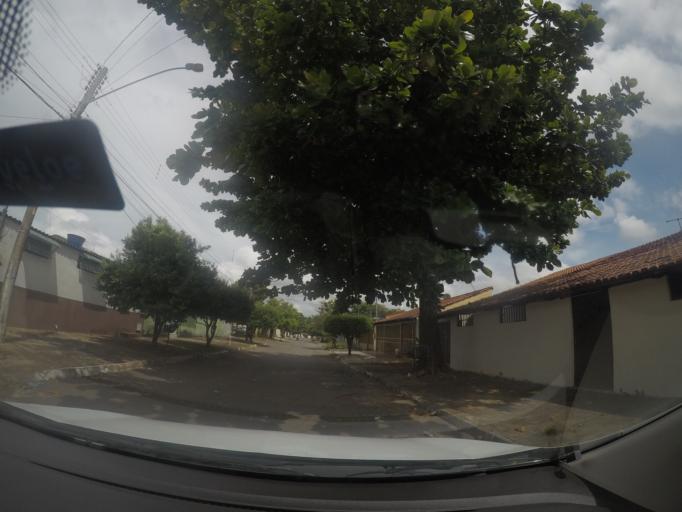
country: BR
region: Goias
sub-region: Goiania
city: Goiania
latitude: -16.7192
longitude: -49.3164
